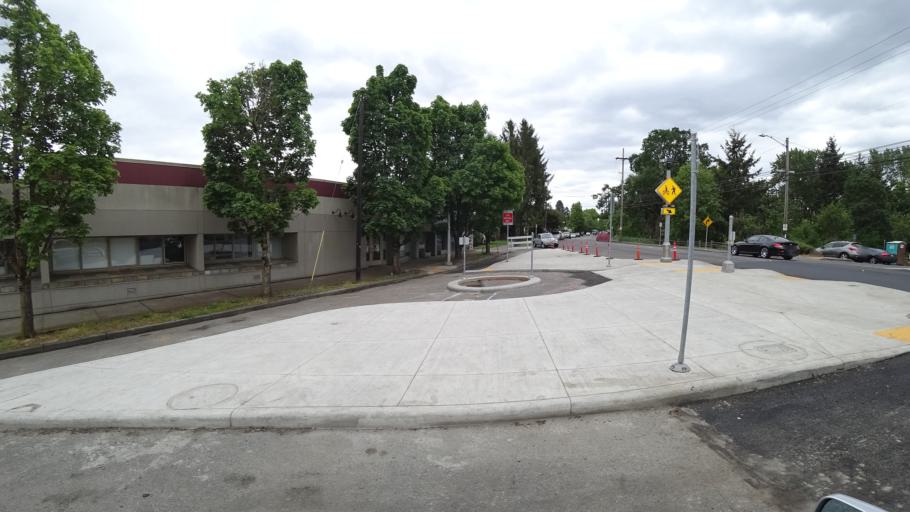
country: US
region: Oregon
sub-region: Clackamas County
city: Milwaukie
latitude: 45.4859
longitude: -122.6496
